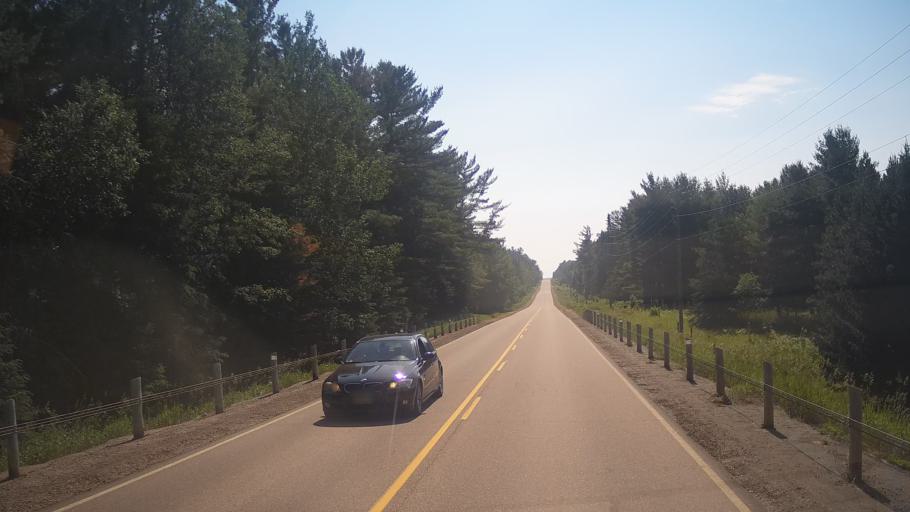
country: CA
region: Ontario
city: Pembroke
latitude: 45.6192
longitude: -77.1693
